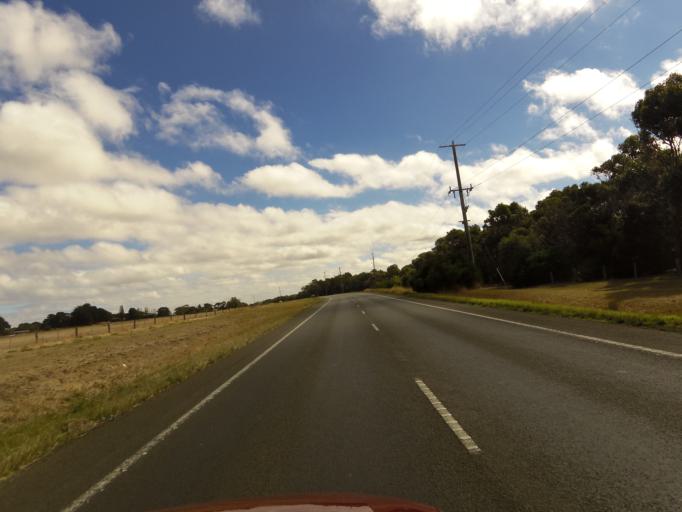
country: AU
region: Victoria
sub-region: Warrnambool
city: Allansford
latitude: -38.3377
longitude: 142.7149
